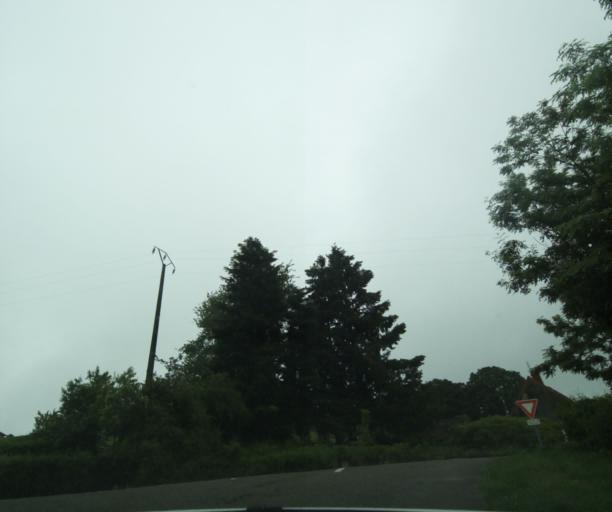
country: FR
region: Bourgogne
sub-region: Departement de Saone-et-Loire
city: Charolles
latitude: 46.4004
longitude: 4.1955
